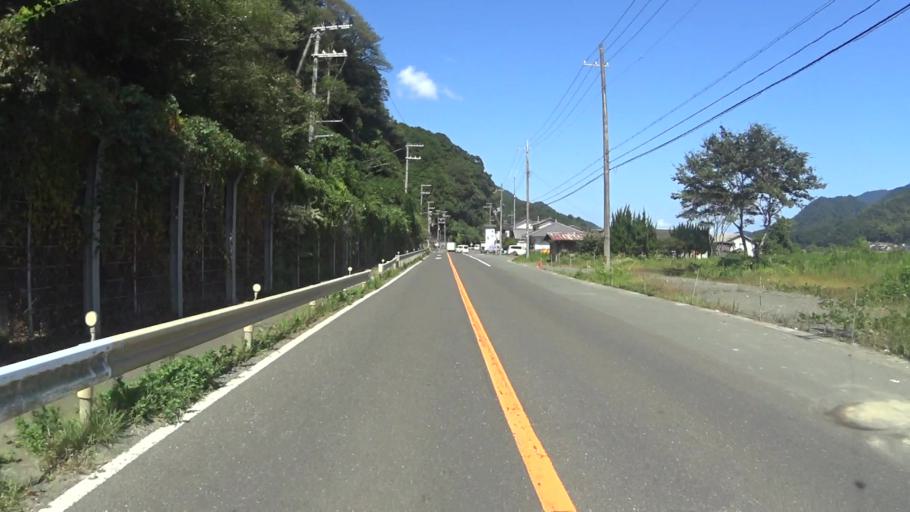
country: JP
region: Kyoto
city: Maizuru
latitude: 35.4718
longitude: 135.2772
